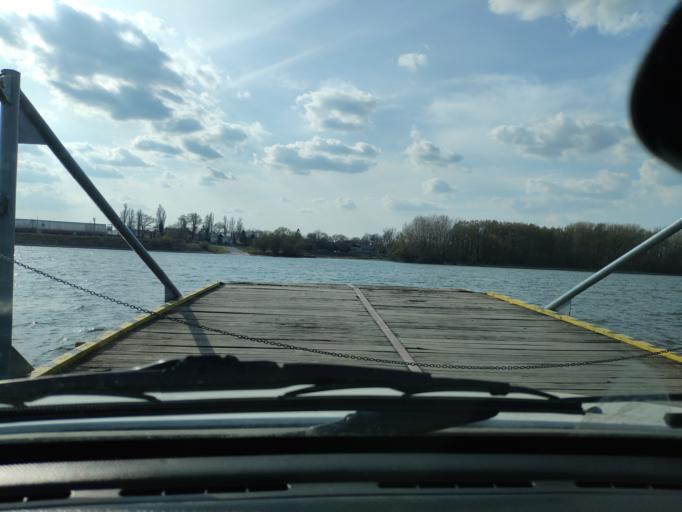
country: HU
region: Fejer
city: Adony
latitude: 47.1133
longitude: 18.8849
